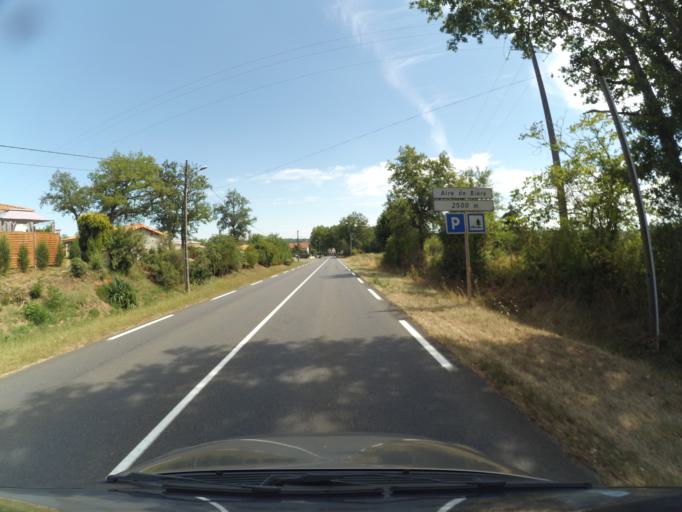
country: FR
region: Poitou-Charentes
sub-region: Departement de la Charente
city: Etagnac
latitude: 45.9359
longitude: 0.7355
